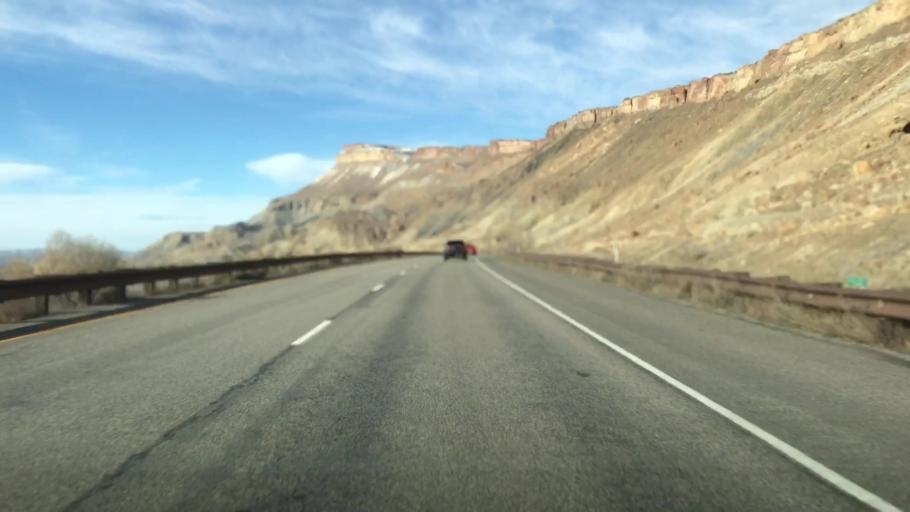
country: US
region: Colorado
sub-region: Mesa County
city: Palisade
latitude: 39.1174
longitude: -108.3578
